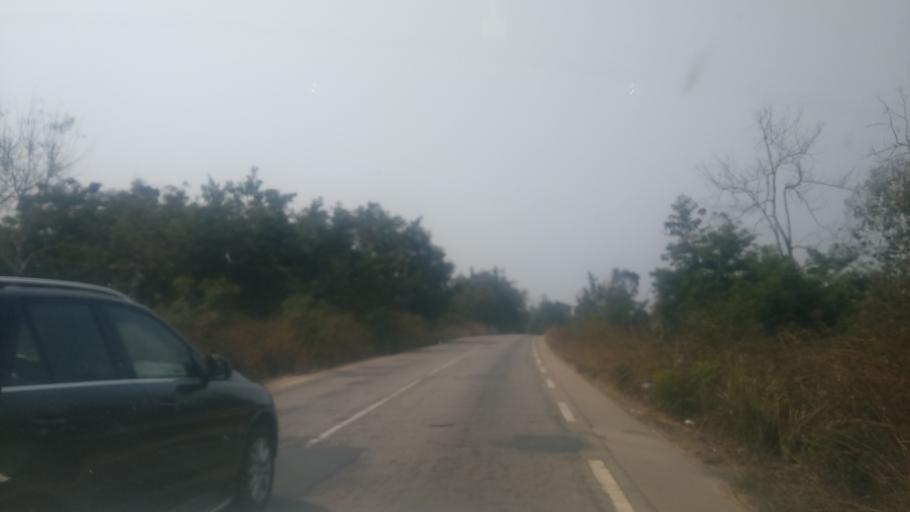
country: CM
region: Centre
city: Bafia
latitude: 4.8385
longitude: 11.0674
